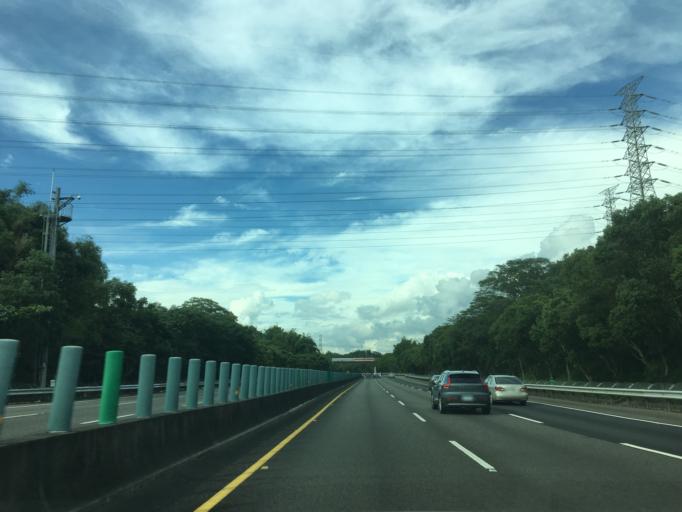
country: TW
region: Taiwan
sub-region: Chiayi
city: Jiayi Shi
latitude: 23.5389
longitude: 120.4955
